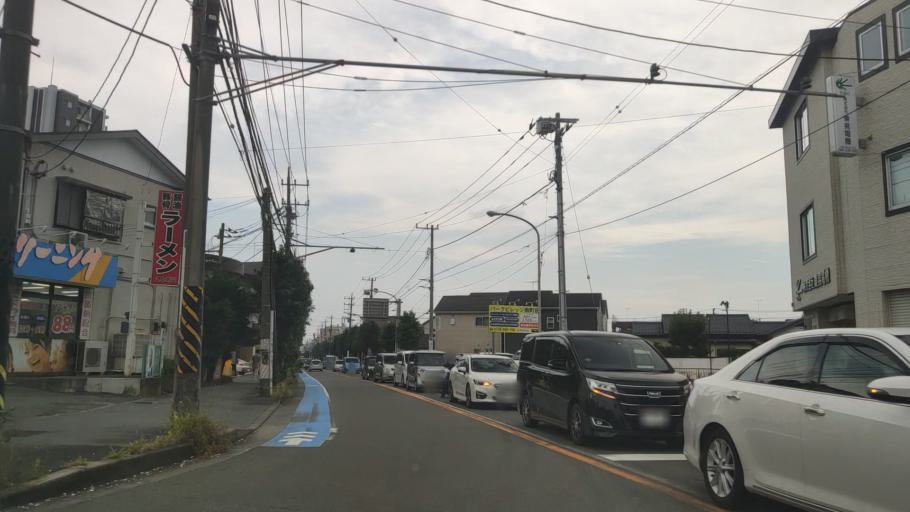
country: JP
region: Kanagawa
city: Minami-rinkan
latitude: 35.5012
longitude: 139.4499
